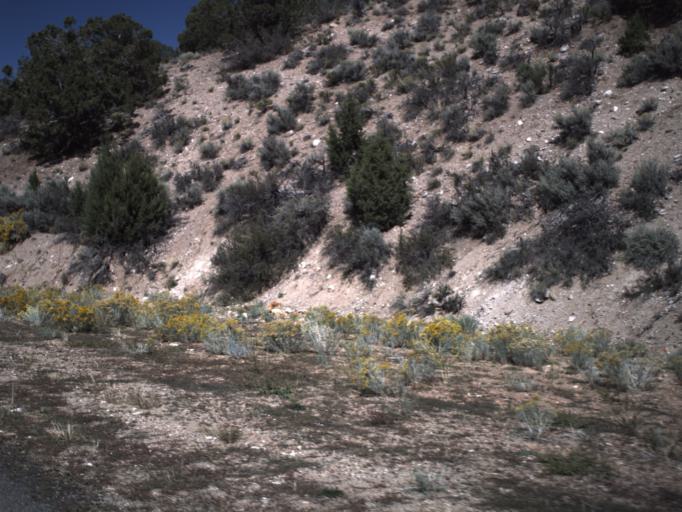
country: US
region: Utah
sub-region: Washington County
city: Enterprise
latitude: 37.5539
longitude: -113.6883
